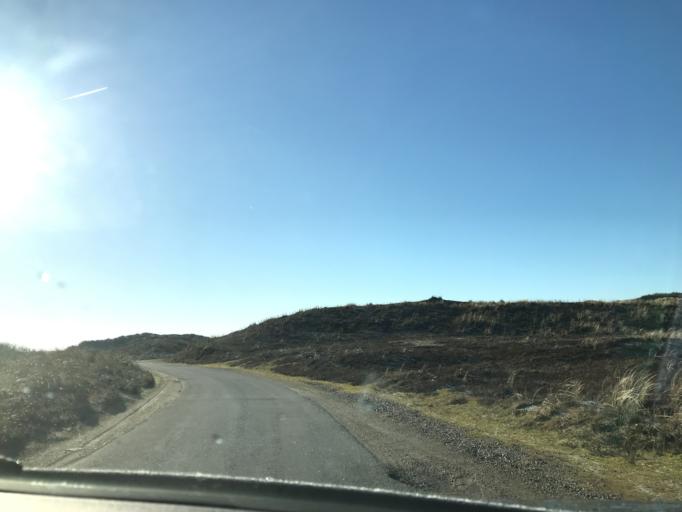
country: DK
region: Central Jutland
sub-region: Ringkobing-Skjern Kommune
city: Hvide Sande
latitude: 55.8141
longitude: 8.1763
